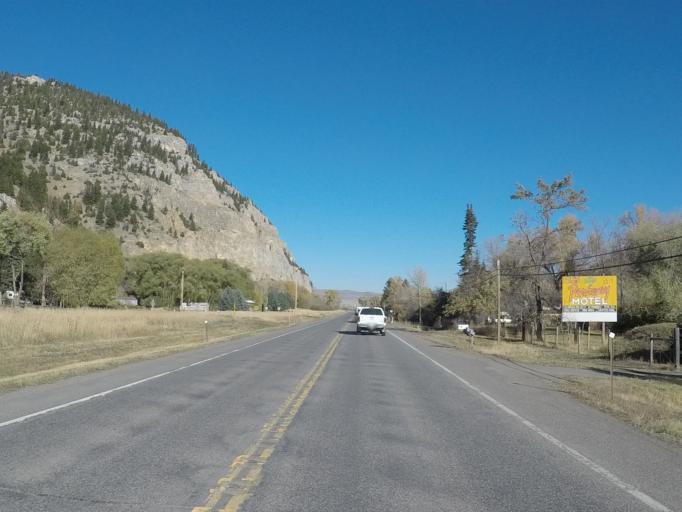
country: US
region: Montana
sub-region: Park County
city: Livingston
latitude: 45.6047
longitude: -110.5747
